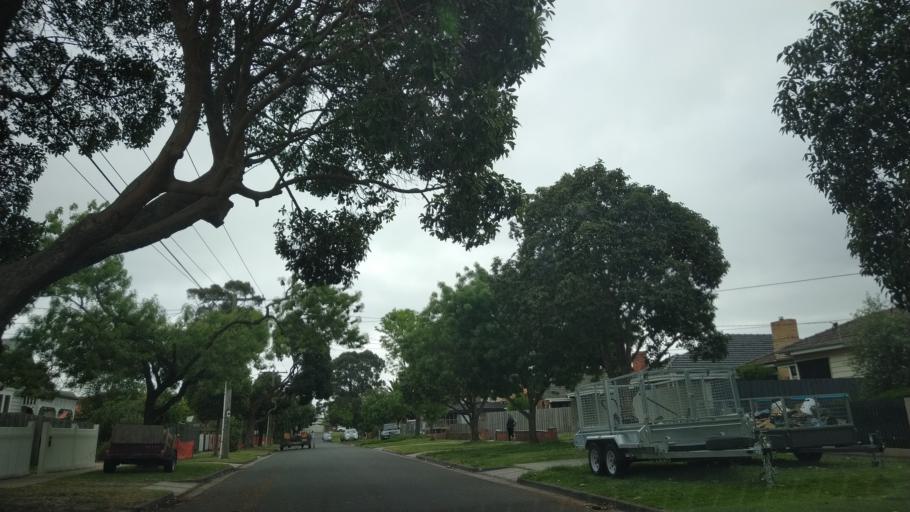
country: AU
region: Victoria
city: Hughesdale
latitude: -37.9023
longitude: 145.0813
